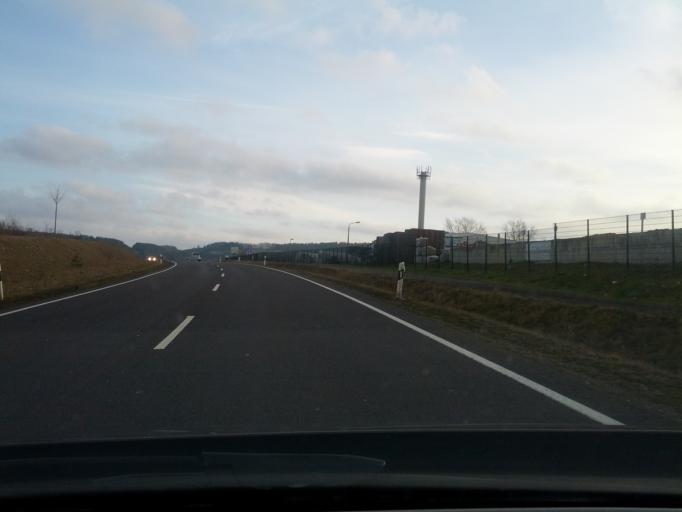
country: DE
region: Thuringia
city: Krauthausen
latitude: 51.0140
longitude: 10.2602
